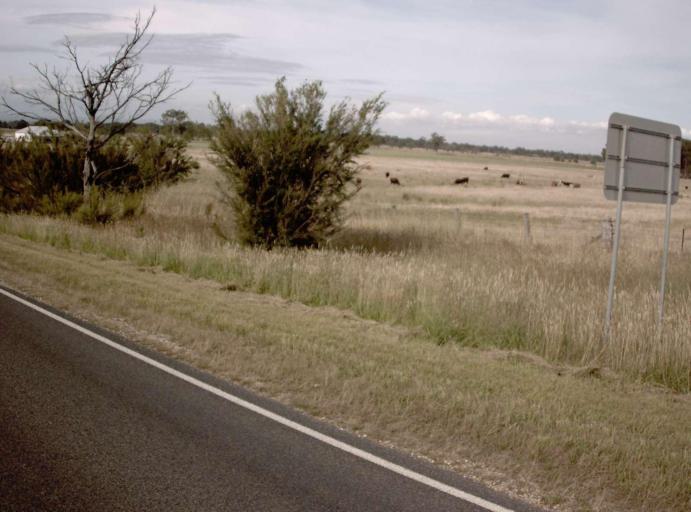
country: AU
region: Victoria
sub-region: Wellington
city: Heyfield
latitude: -38.0222
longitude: 146.6696
